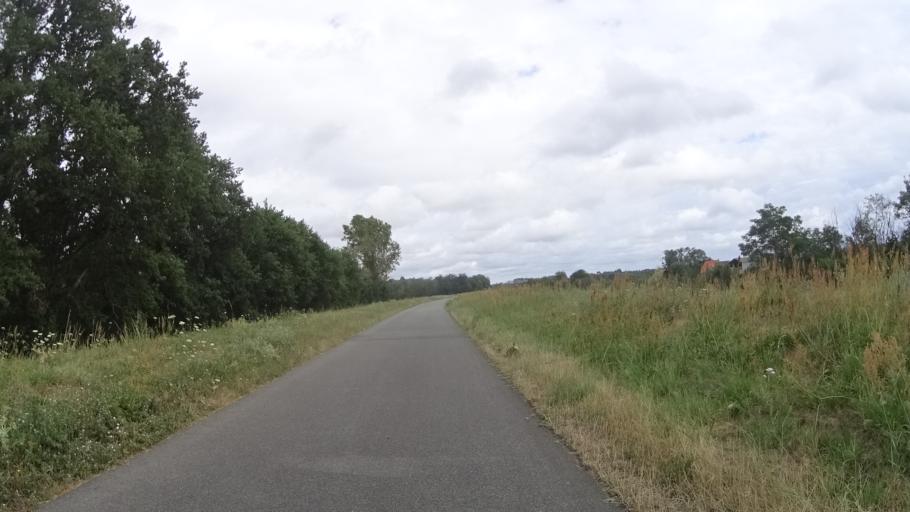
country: FR
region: Centre
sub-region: Departement du Loiret
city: Saint-Ay
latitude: 47.8477
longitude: 1.7522
